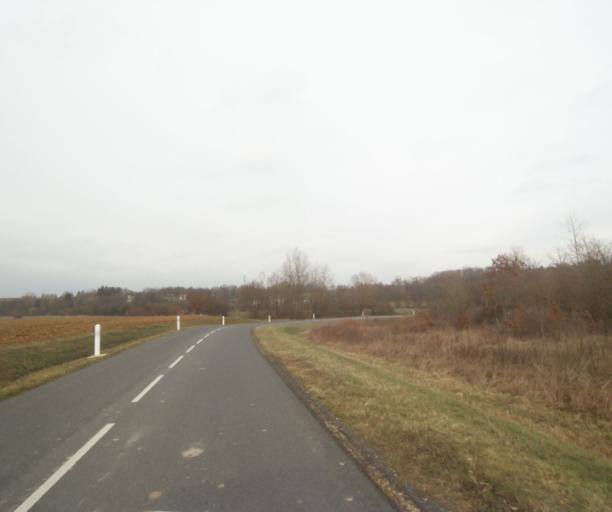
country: FR
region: Champagne-Ardenne
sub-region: Departement de la Marne
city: Pargny-sur-Saulx
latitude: 48.7446
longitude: 4.8596
